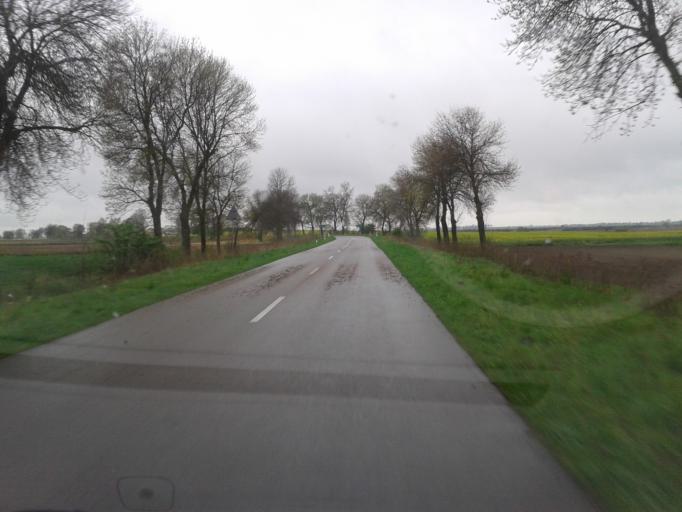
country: PL
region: Lublin Voivodeship
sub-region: Powiat tomaszowski
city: Ulhowek
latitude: 50.4227
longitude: 23.7758
